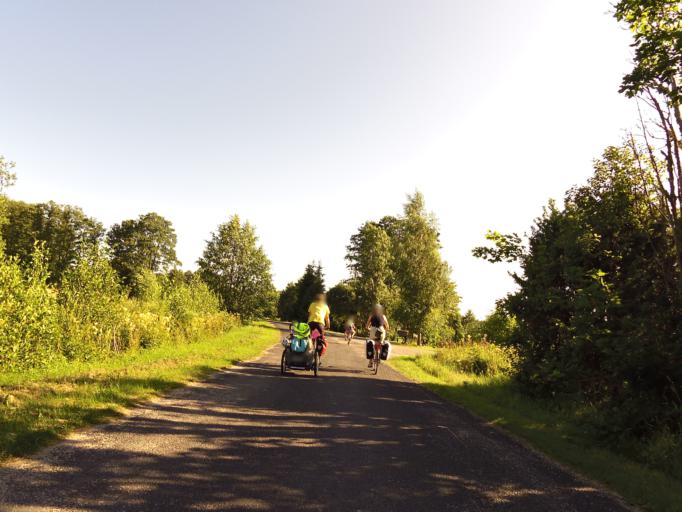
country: EE
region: Hiiumaa
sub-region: Kaerdla linn
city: Kardla
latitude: 58.7795
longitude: 22.4859
